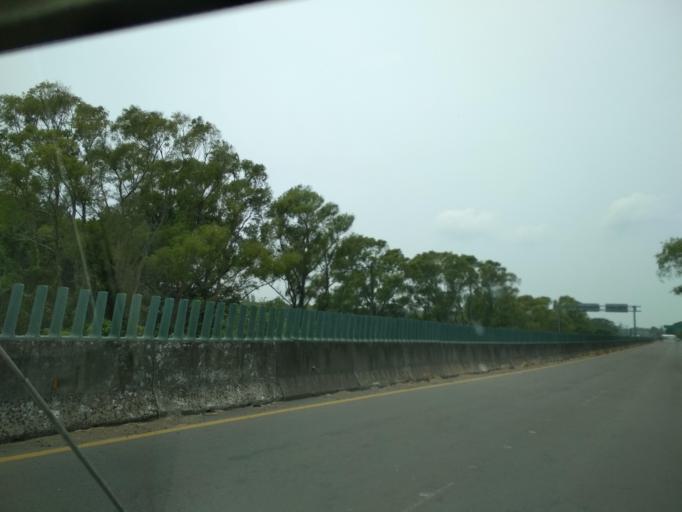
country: MX
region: Veracruz
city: Paso del Toro
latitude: 19.0278
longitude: -96.1409
